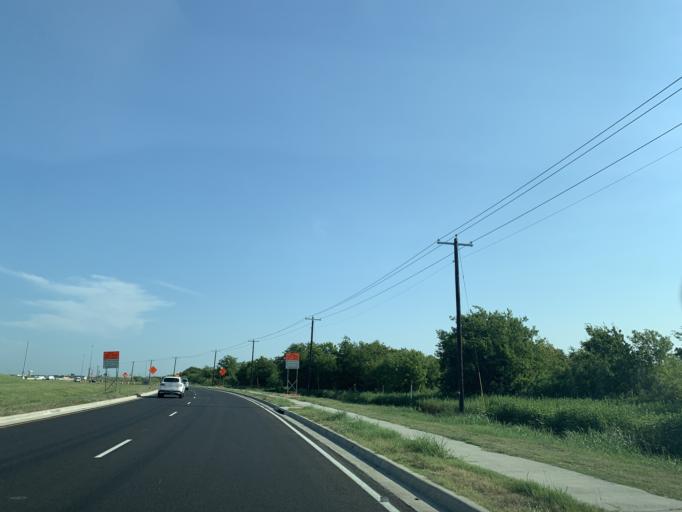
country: US
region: Texas
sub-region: Tarrant County
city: Blue Mound
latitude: 32.8834
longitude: -97.3148
